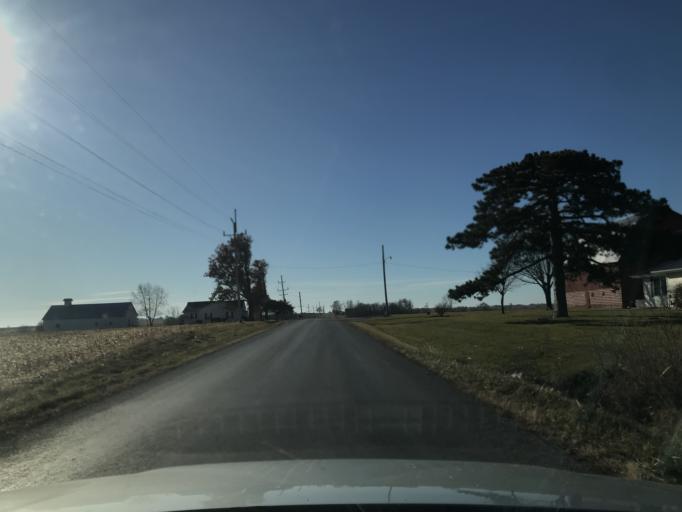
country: US
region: Illinois
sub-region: Hancock County
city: Carthage
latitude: 40.4918
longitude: -91.1778
